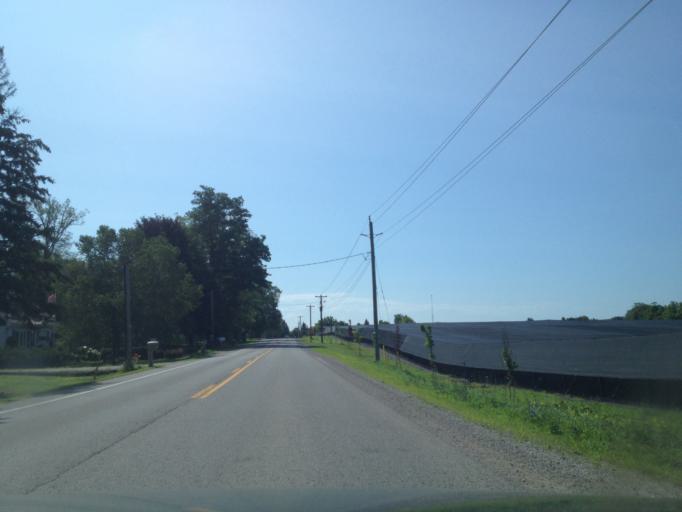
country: CA
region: Ontario
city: Norfolk County
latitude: 42.7692
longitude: -80.3919
